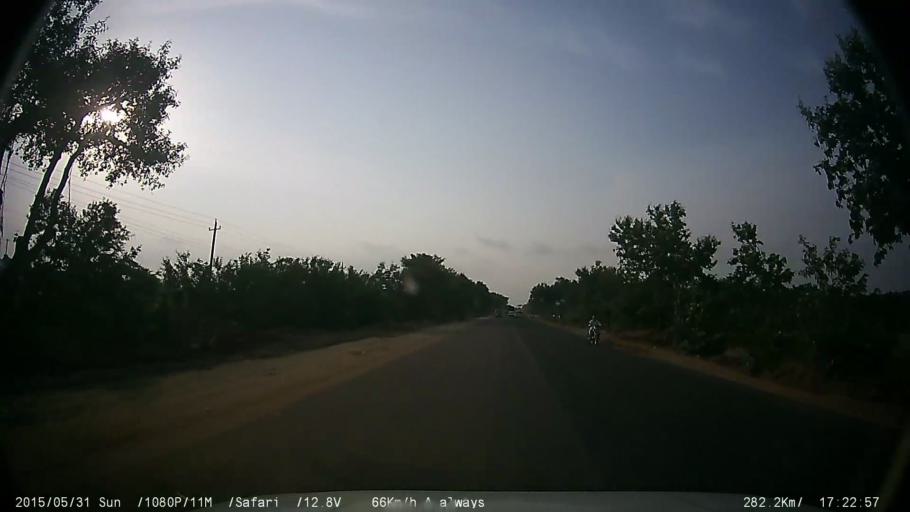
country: IN
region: Karnataka
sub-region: Chamrajnagar
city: Gundlupet
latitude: 11.8352
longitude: 76.6763
